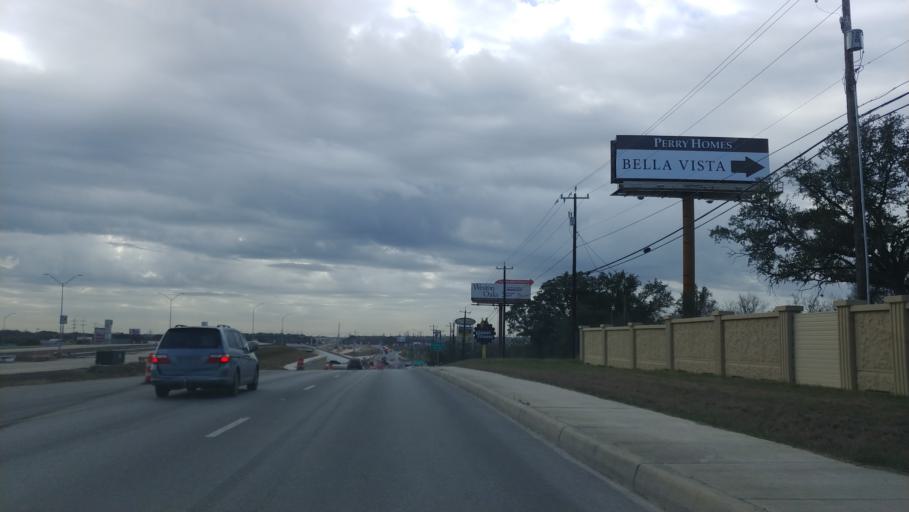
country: US
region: Texas
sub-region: Bexar County
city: Lackland Air Force Base
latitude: 29.4385
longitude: -98.7120
